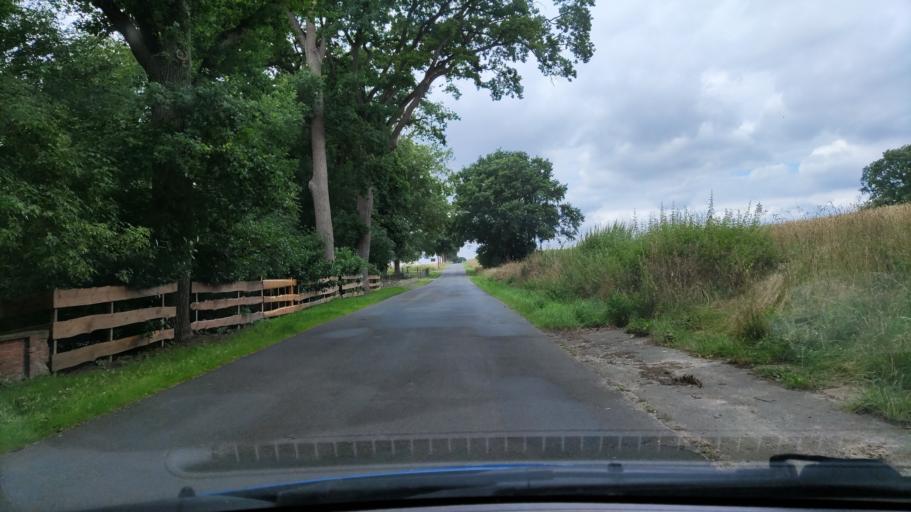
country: DE
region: Lower Saxony
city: Romstedt
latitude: 53.0834
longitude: 10.6782
